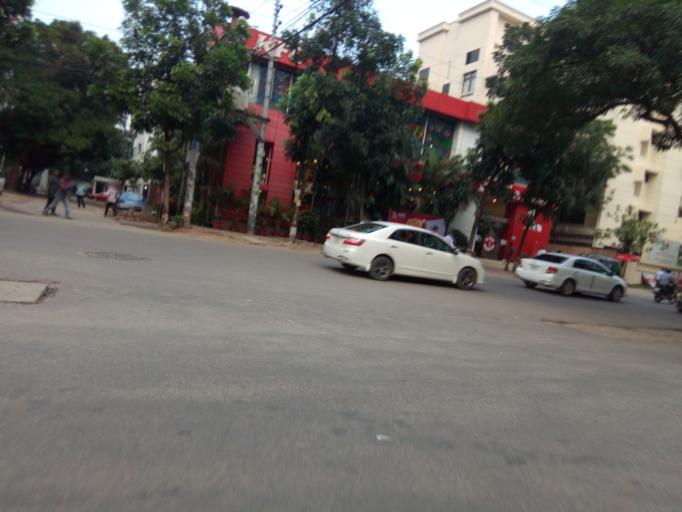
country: BD
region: Dhaka
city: Paltan
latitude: 23.7755
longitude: 90.4162
